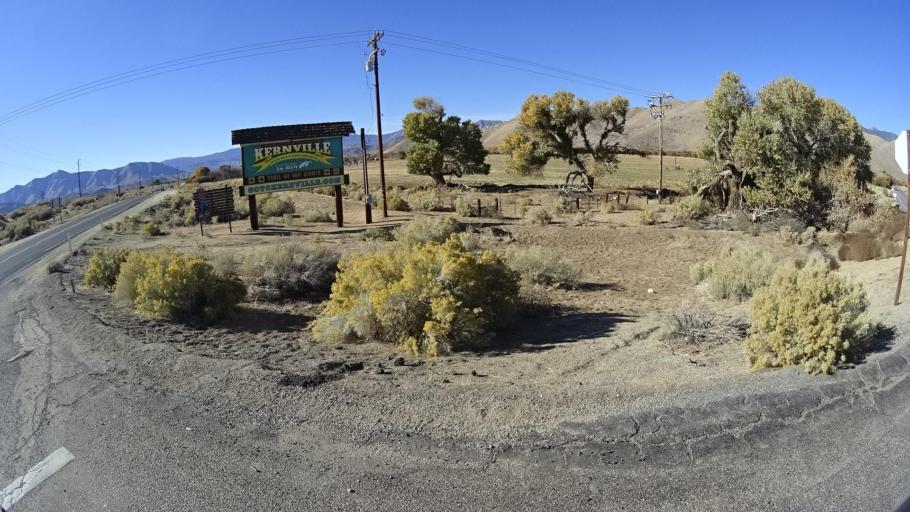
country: US
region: California
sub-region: Kern County
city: Weldon
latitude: 35.6571
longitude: -118.3230
